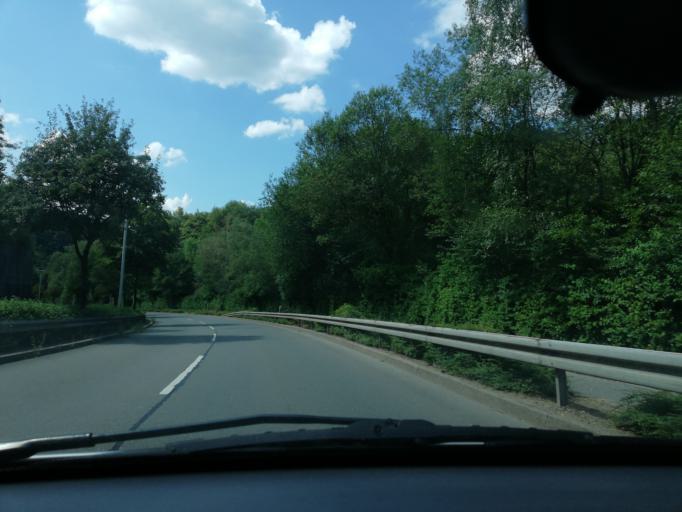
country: DE
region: North Rhine-Westphalia
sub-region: Regierungsbezirk Dusseldorf
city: Wuppertal
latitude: 51.2442
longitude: 7.1684
